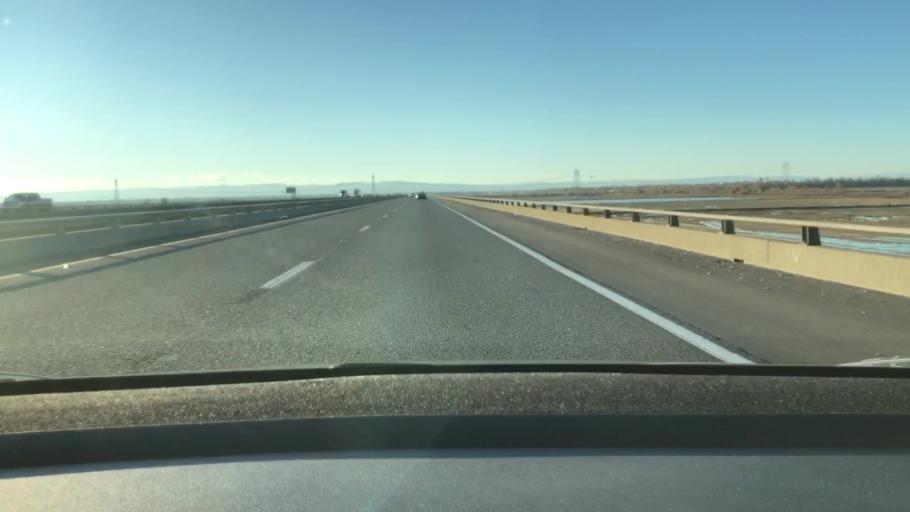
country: US
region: California
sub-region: Yolo County
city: Woodland
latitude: 38.6727
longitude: -121.6658
